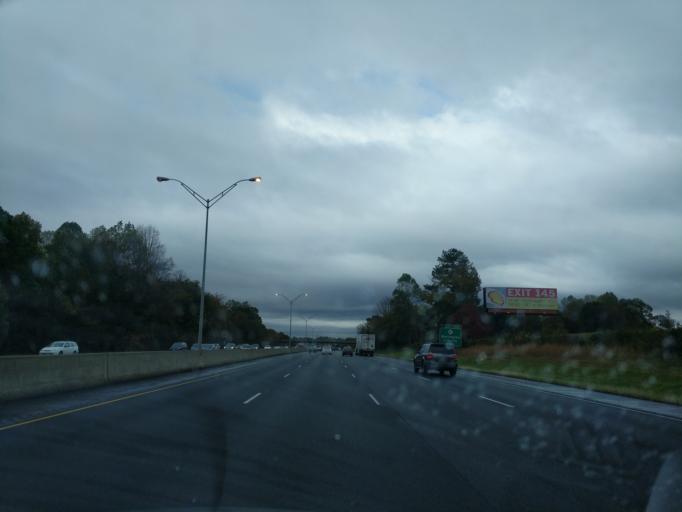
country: US
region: North Carolina
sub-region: Alamance County
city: Burlington
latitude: 36.0648
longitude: -79.4549
